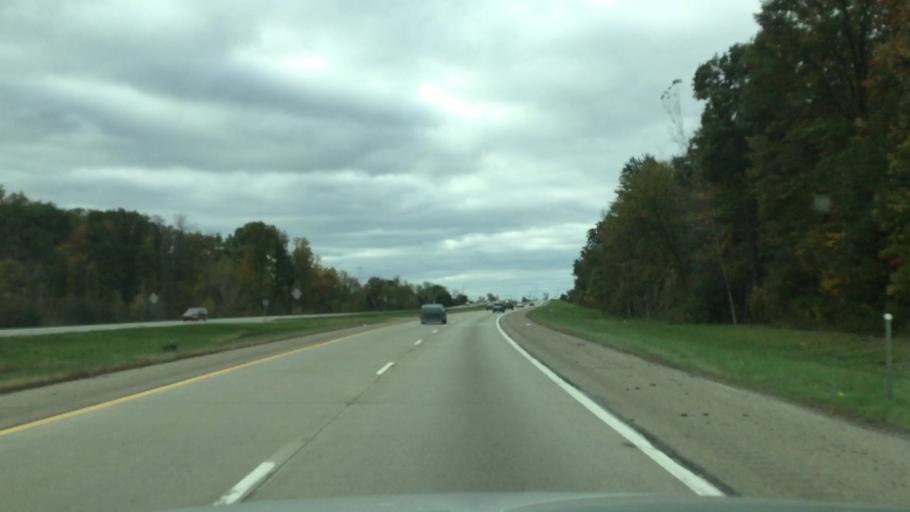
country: US
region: Michigan
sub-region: Macomb County
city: Romeo
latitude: 42.7940
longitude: -83.0017
